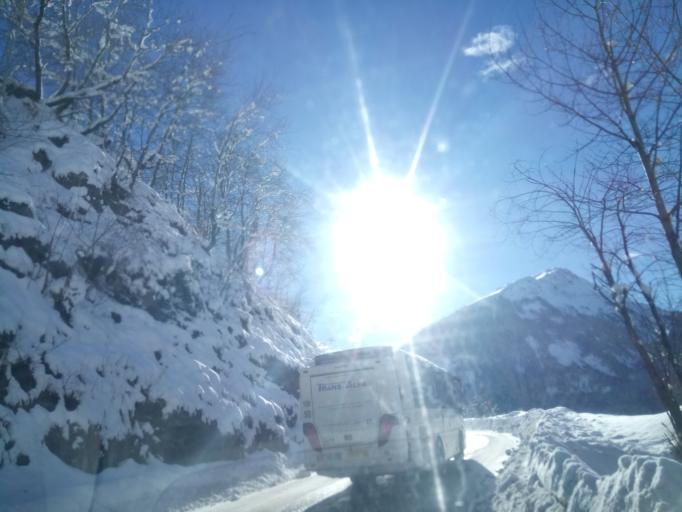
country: FR
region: Rhone-Alpes
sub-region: Departement de la Savoie
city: Saint-Jean-de-Maurienne
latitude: 45.2494
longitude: 6.2878
